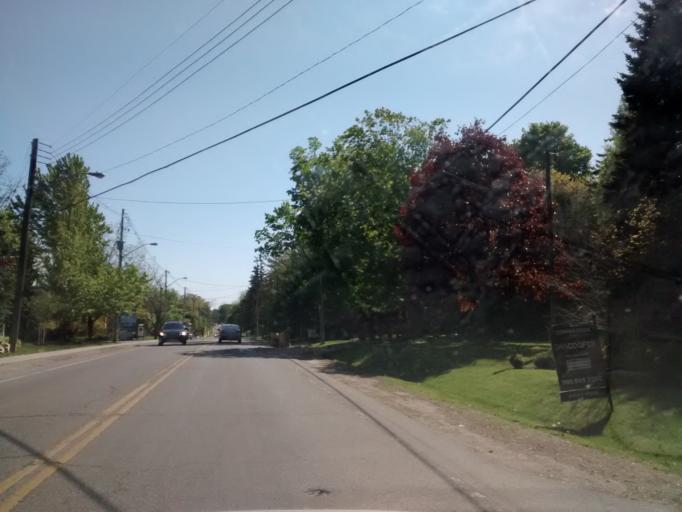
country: CA
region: Ontario
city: Oakville
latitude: 43.4319
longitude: -79.6831
